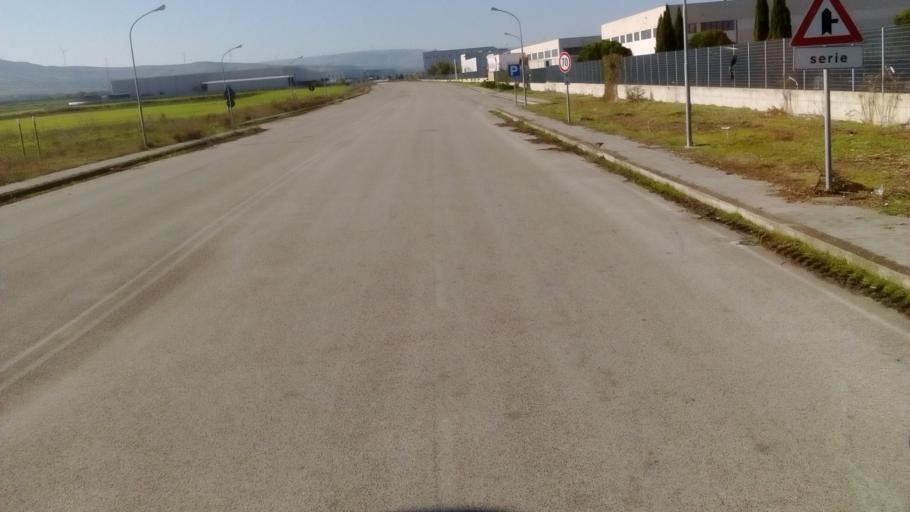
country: IT
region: Basilicate
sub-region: Provincia di Potenza
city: Melfi
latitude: 41.0780
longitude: 15.6663
